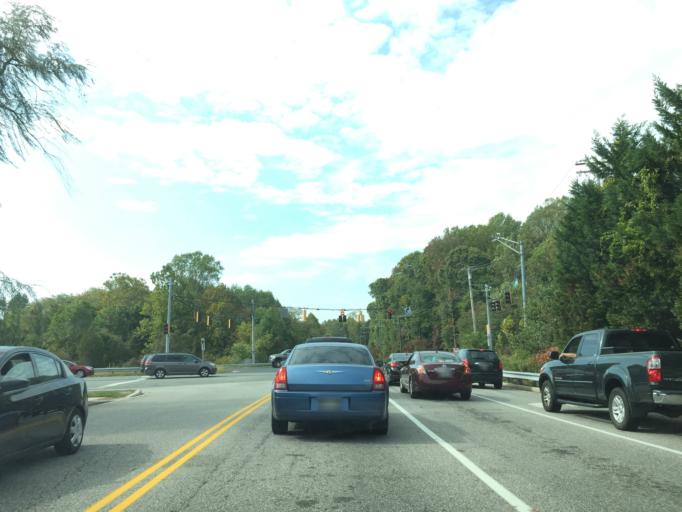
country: US
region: Maryland
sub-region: Harford County
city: Bel Air South
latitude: 39.4788
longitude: -76.3184
